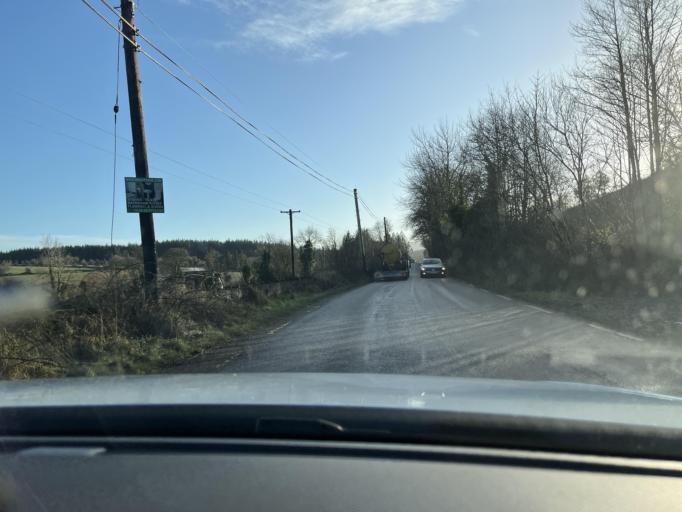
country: IE
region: Connaught
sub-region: County Leitrim
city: Manorhamilton
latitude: 54.1829
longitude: -8.1574
